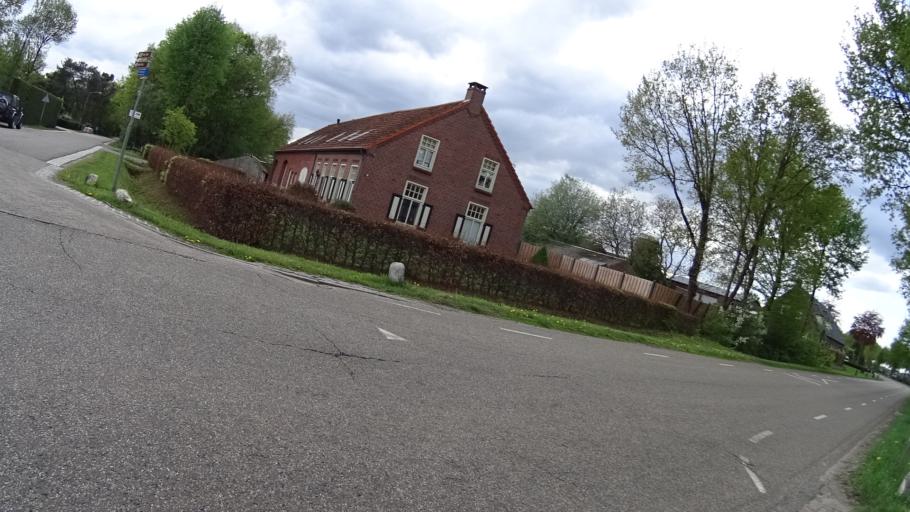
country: NL
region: North Brabant
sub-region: Gemeente Boekel
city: Boekel
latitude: 51.5946
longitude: 5.6960
